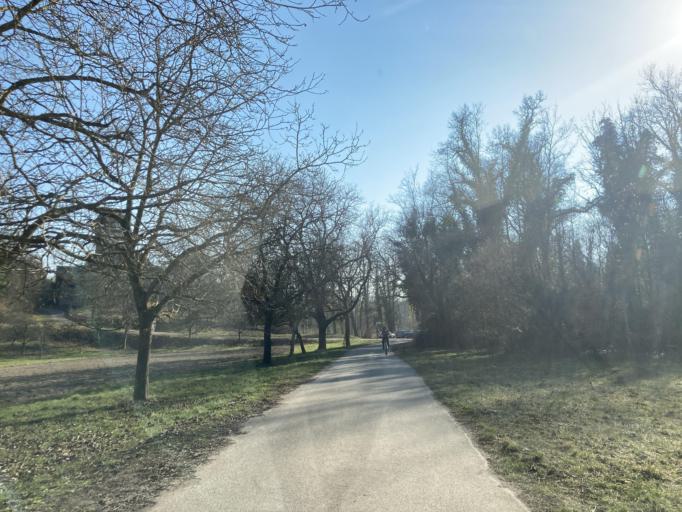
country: DE
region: Baden-Wuerttemberg
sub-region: Freiburg Region
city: Sasbach
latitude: 48.1158
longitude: 7.5835
